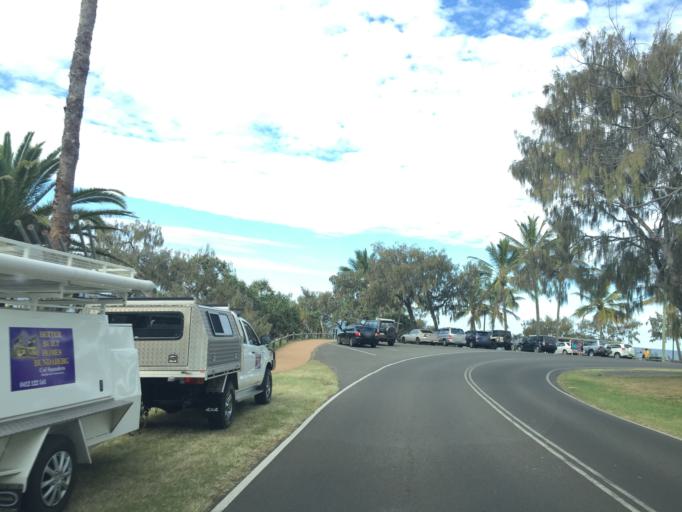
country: AU
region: Queensland
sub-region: Bundaberg
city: Bundaberg
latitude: -24.8265
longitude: 152.4657
